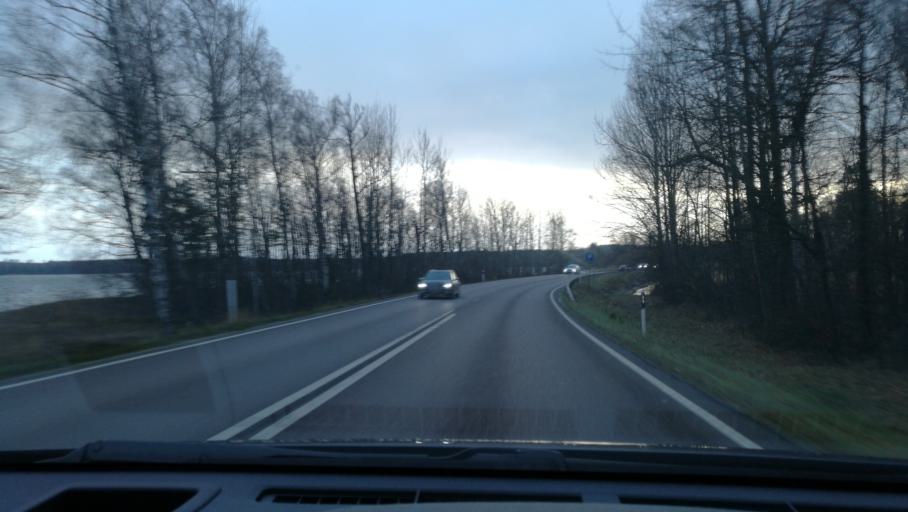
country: SE
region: Vaestmanland
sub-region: Kungsors Kommun
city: Kungsoer
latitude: 59.2511
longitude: 16.1086
